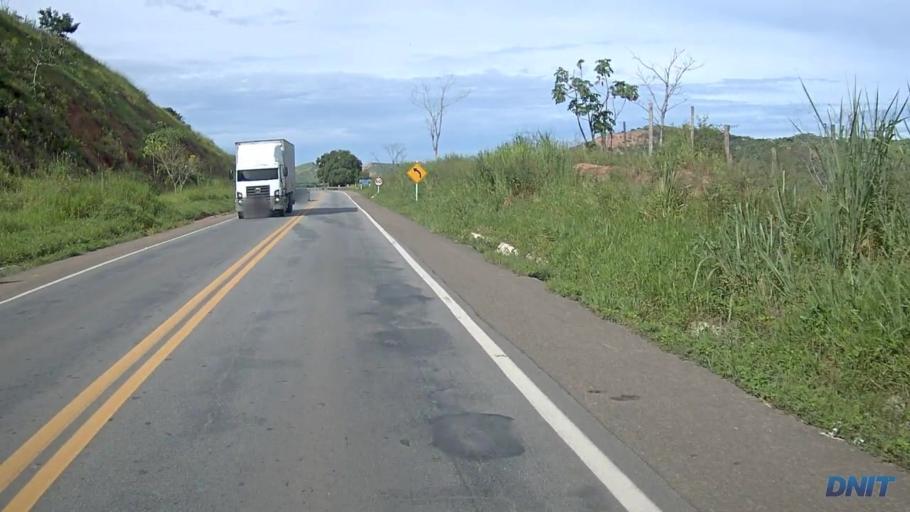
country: BR
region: Minas Gerais
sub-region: Belo Oriente
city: Belo Oriente
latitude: -19.1611
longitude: -42.2401
